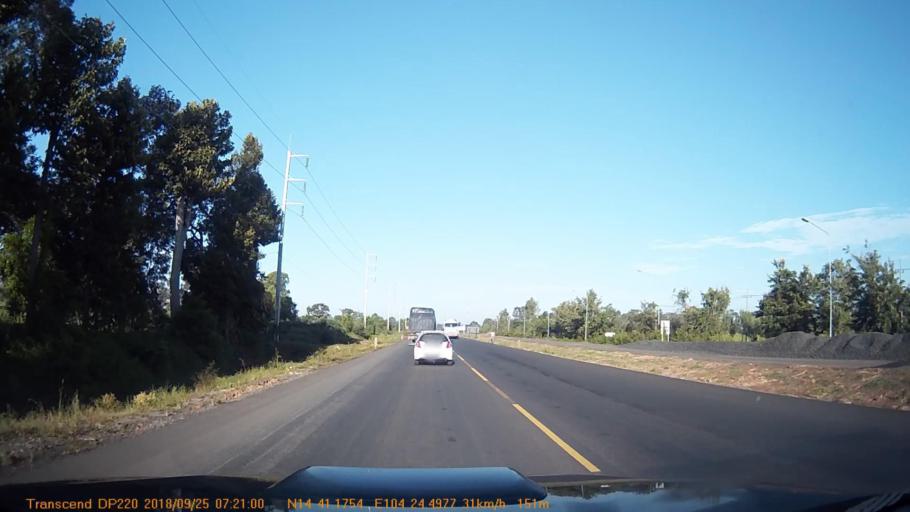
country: TH
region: Sisaket
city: Khun Han
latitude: 14.6862
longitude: 104.4080
